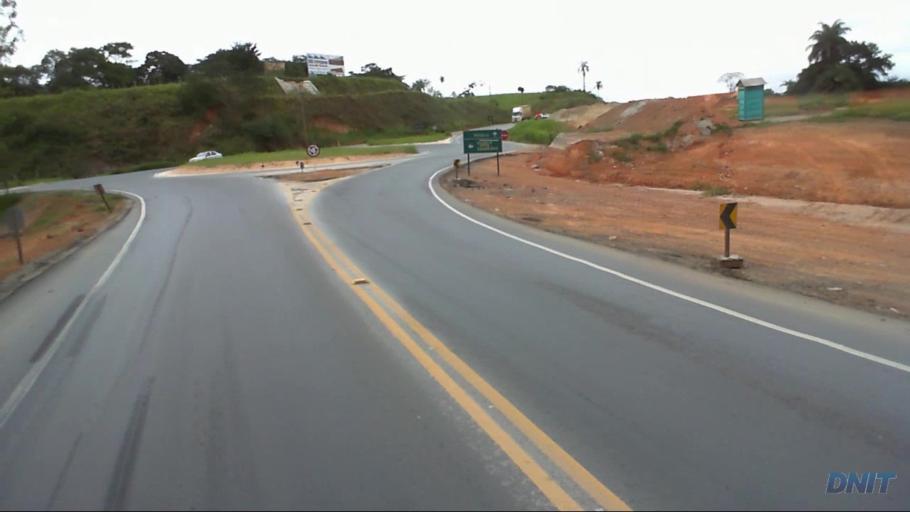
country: BR
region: Minas Gerais
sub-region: Barao De Cocais
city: Barao de Cocais
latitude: -19.7523
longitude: -43.4755
